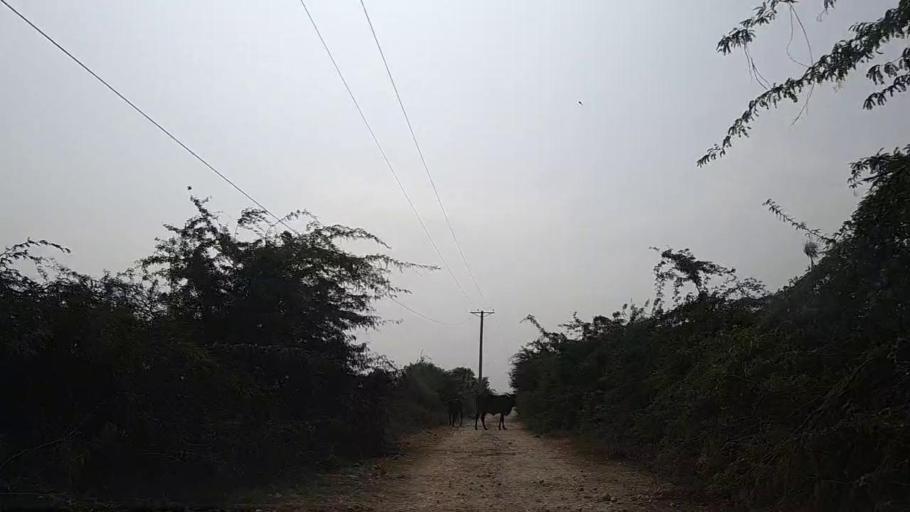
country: PK
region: Sindh
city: Mirpur Sakro
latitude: 24.6331
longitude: 67.7472
